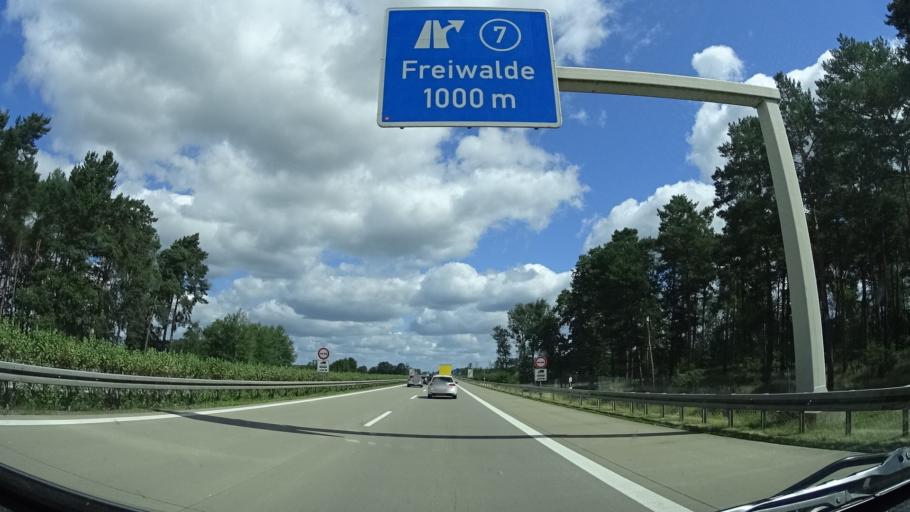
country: DE
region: Brandenburg
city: Kasel-Golzig
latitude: 51.9444
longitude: 13.7641
